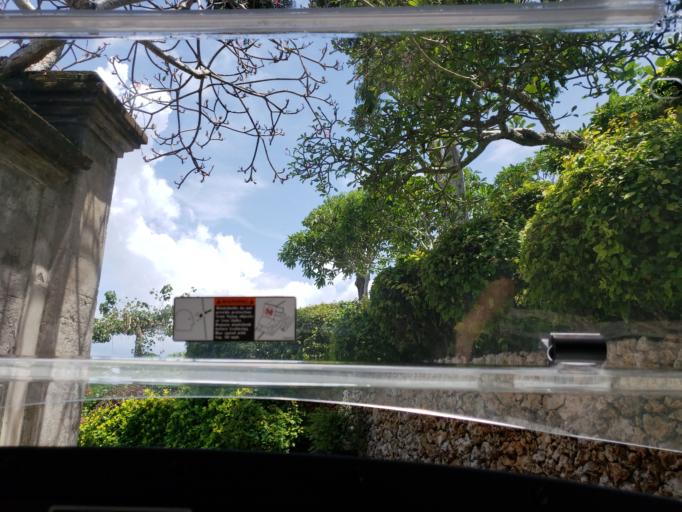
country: ID
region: Bali
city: Jimbaran
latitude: -8.7825
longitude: 115.1586
